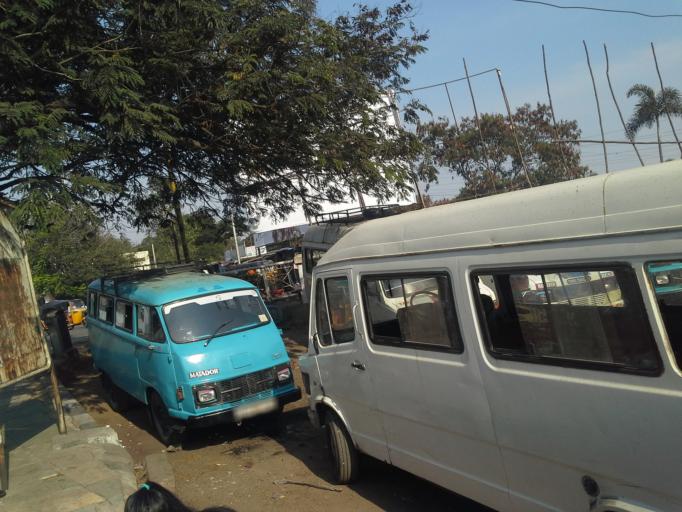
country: IN
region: Telangana
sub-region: Hyderabad
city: Hyderabad
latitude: 17.3725
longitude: 78.4759
